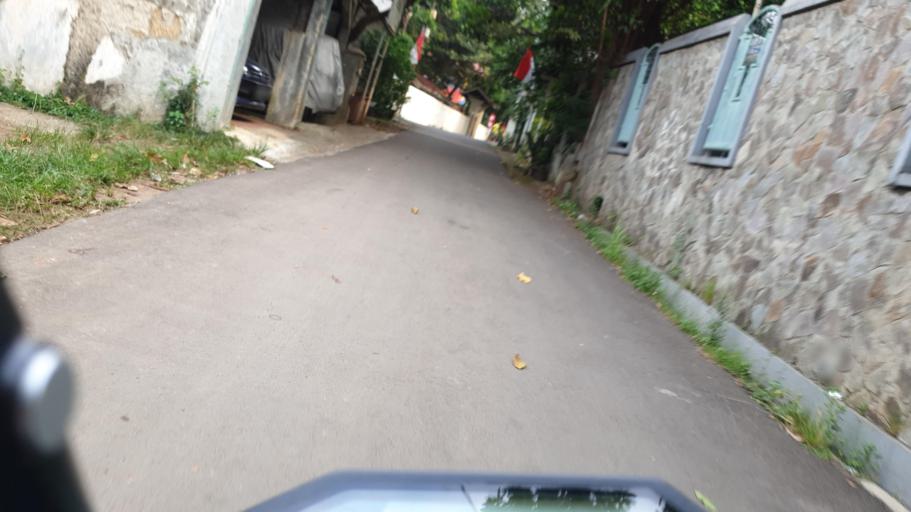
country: ID
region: West Java
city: Depok
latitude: -6.3375
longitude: 106.8309
